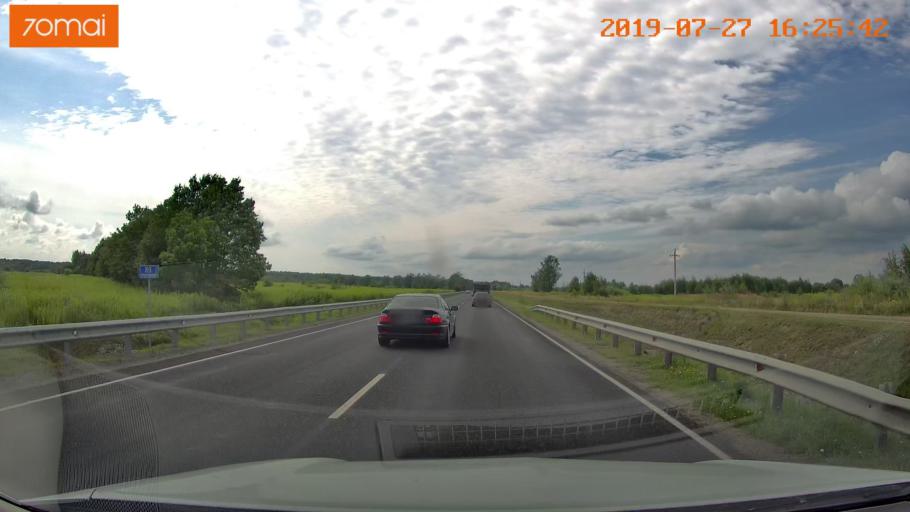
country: RU
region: Kaliningrad
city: Zheleznodorozhnyy
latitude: 54.6381
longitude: 21.4256
